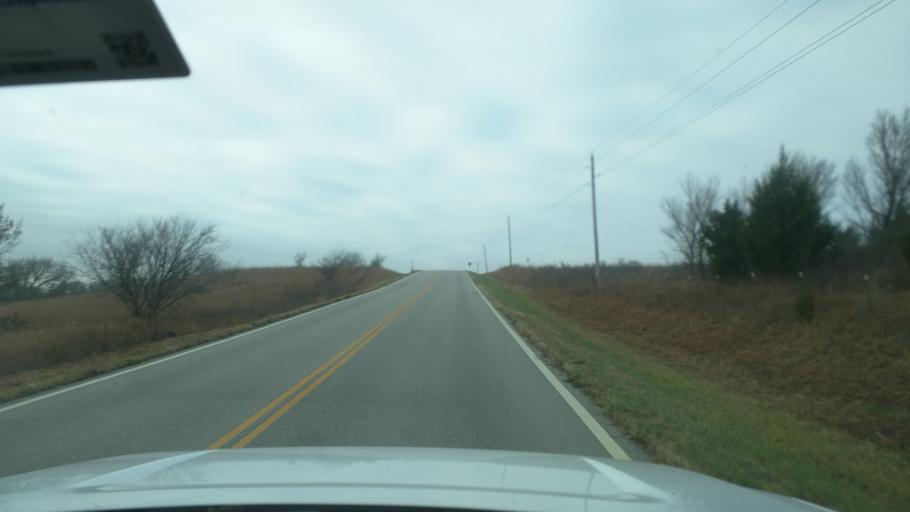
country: US
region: Kansas
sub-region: Greenwood County
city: Eureka
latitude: 37.6915
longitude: -96.2300
